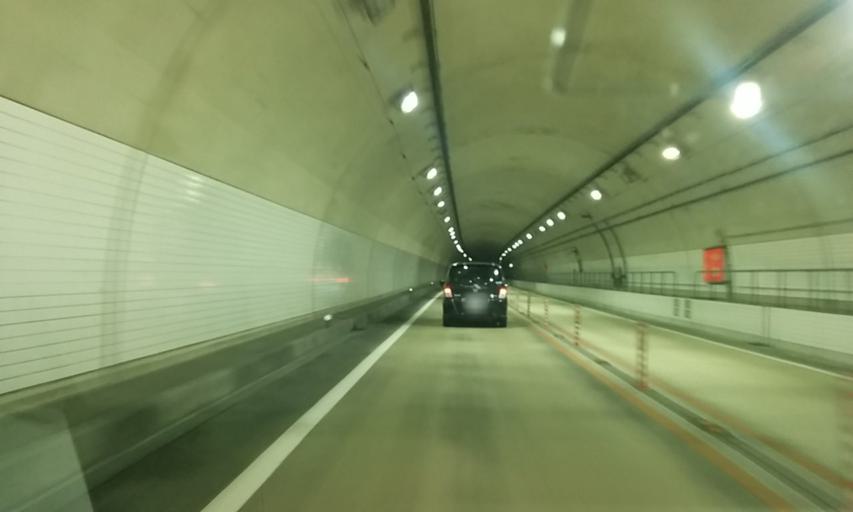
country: JP
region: Kyoto
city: Miyazu
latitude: 35.5532
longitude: 135.1327
